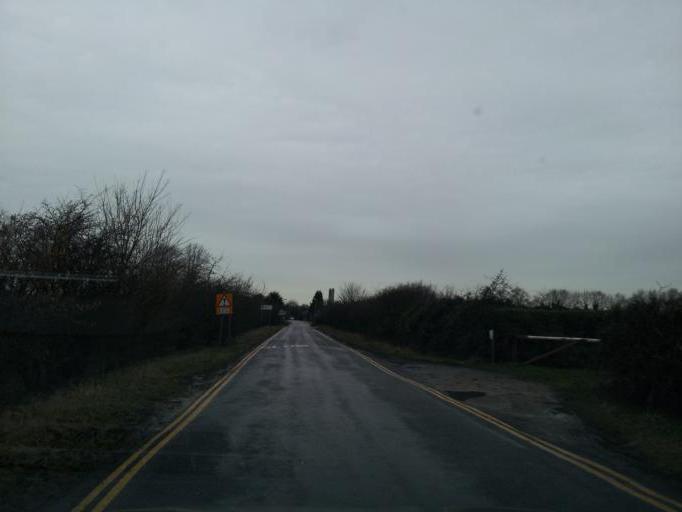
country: GB
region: England
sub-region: Cambridgeshire
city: Cambridge
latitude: 52.1733
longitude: 0.1556
